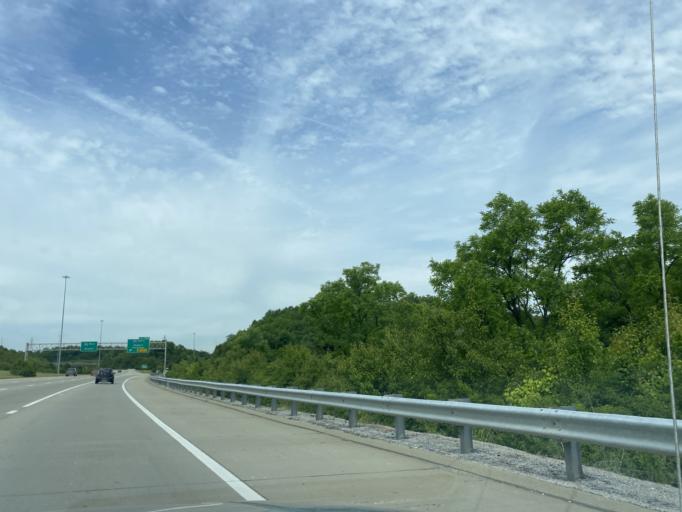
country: US
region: Kentucky
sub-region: Campbell County
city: Highland Heights
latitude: 39.0481
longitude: -84.4544
